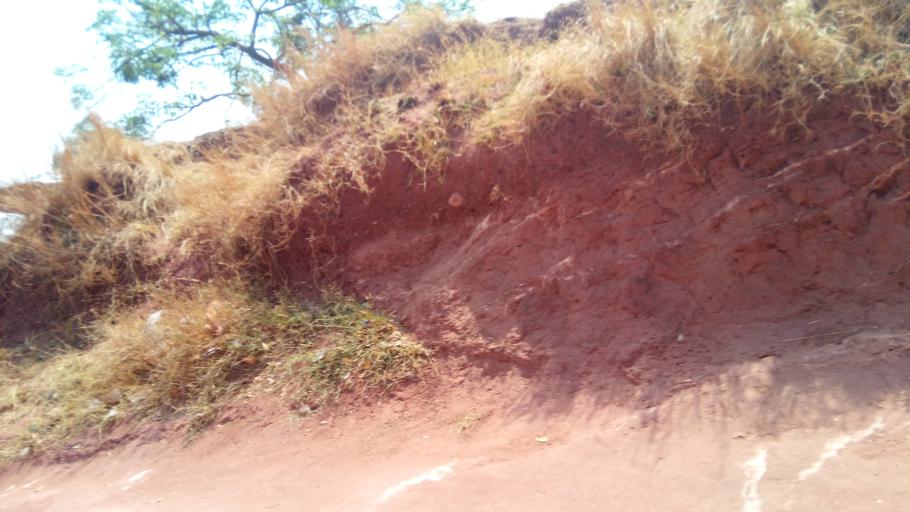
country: CD
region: Katanga
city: Kalemie
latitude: -5.9330
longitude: 29.1884
